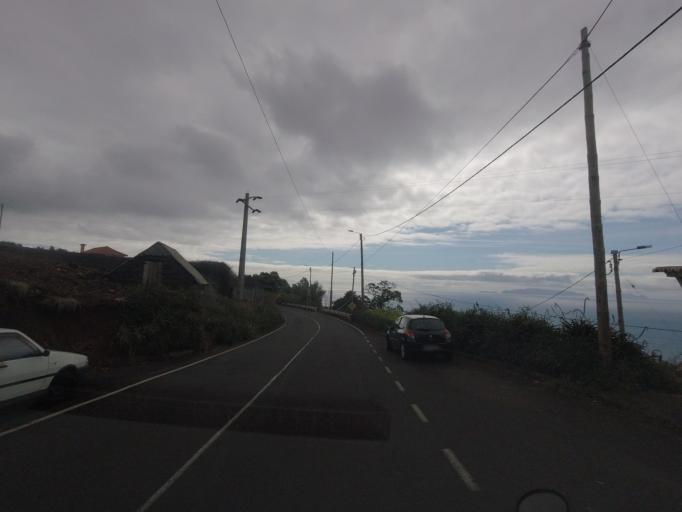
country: PT
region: Madeira
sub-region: Machico
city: Machico
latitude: 32.7013
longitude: -16.7851
